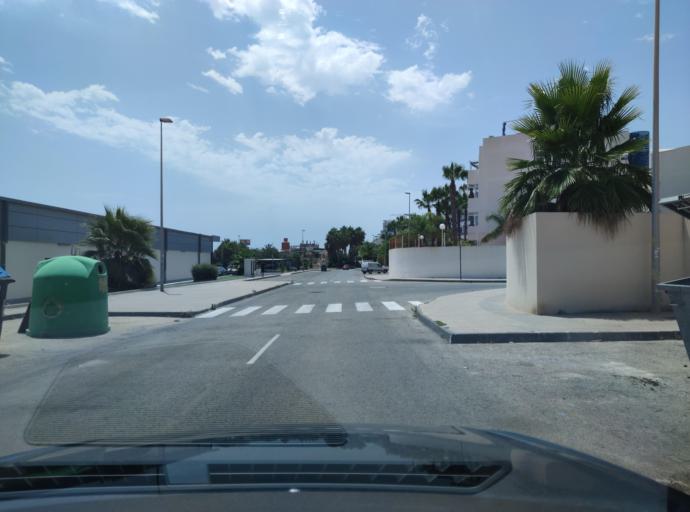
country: ES
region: Valencia
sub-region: Provincia de Alicante
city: Torrevieja
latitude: 37.9393
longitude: -0.7211
